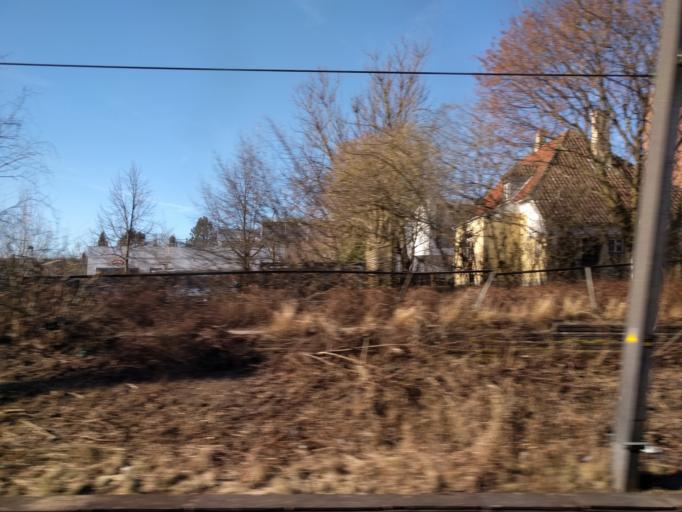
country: DK
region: Capital Region
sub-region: Horsholm Kommune
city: Horsholm
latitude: 55.8837
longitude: 12.5299
